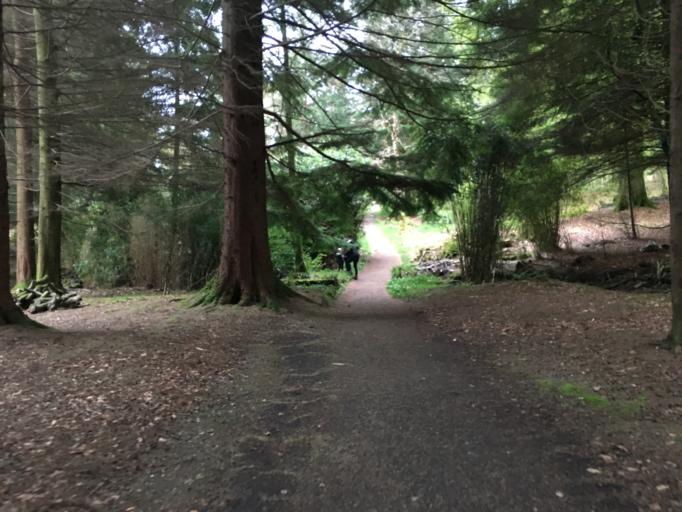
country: GB
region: Scotland
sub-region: Argyll and Bute
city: Rothesay
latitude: 55.7981
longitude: -5.0199
